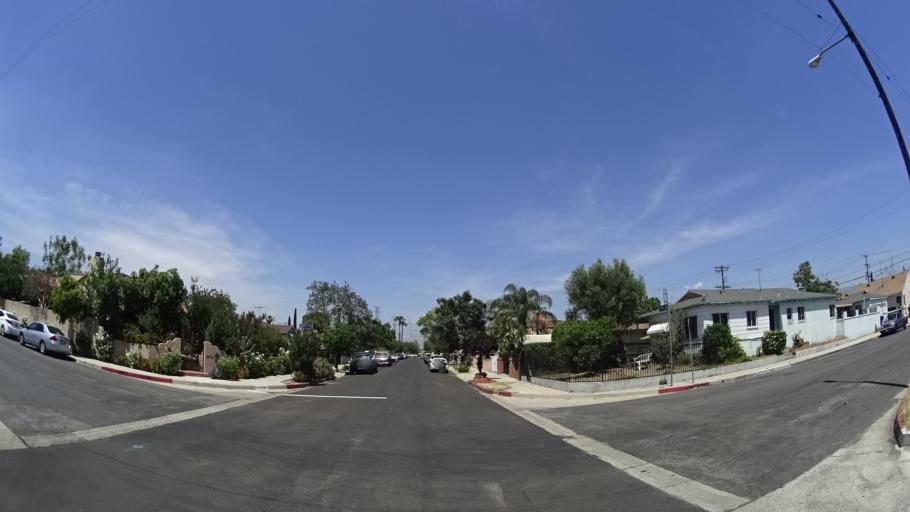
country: US
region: California
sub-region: Los Angeles County
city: North Hollywood
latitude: 34.1811
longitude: -118.3713
